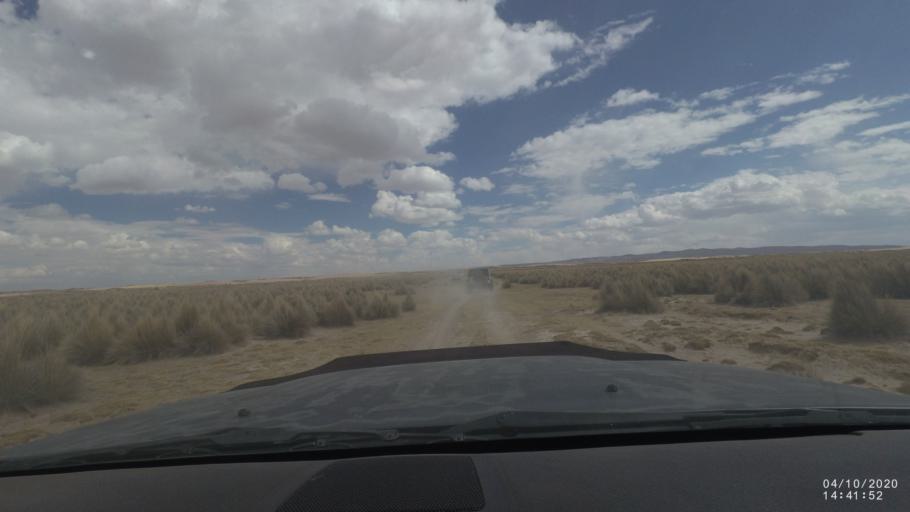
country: BO
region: Oruro
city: Poopo
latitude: -18.6841
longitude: -67.4908
